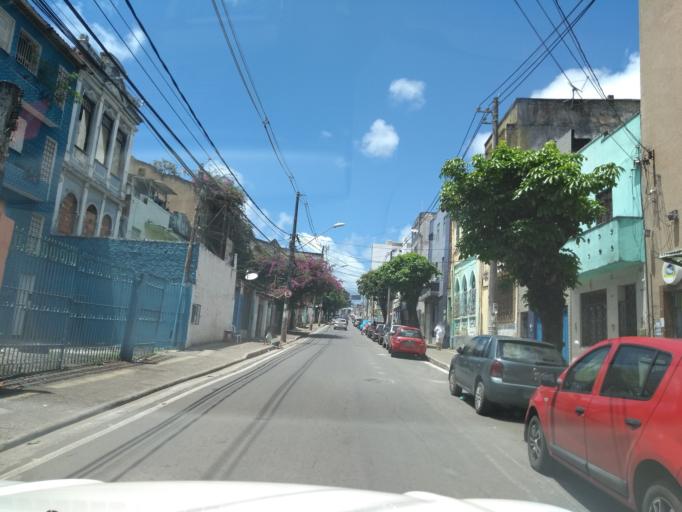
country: BR
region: Bahia
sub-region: Salvador
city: Salvador
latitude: -12.9775
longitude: -38.5094
